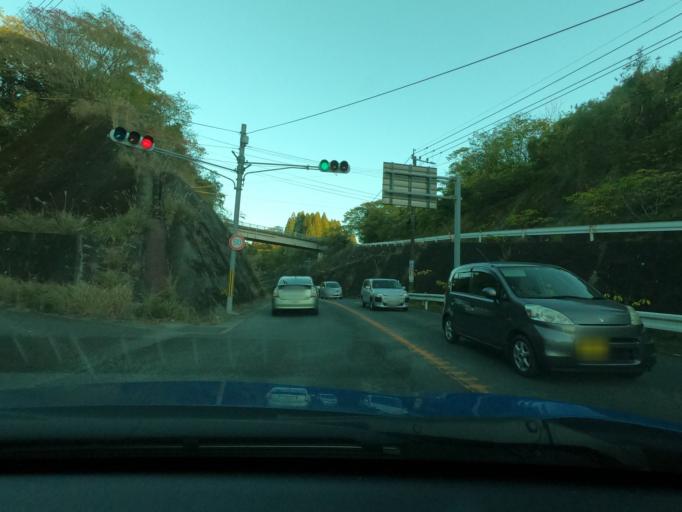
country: JP
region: Kagoshima
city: Satsumasendai
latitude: 31.7963
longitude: 130.4213
